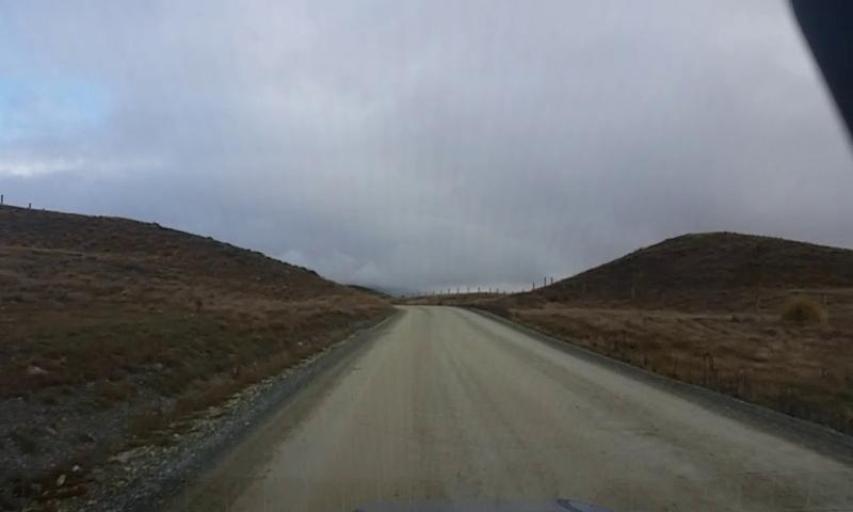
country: NZ
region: Canterbury
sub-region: Ashburton District
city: Methven
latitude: -43.6148
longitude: 171.1475
